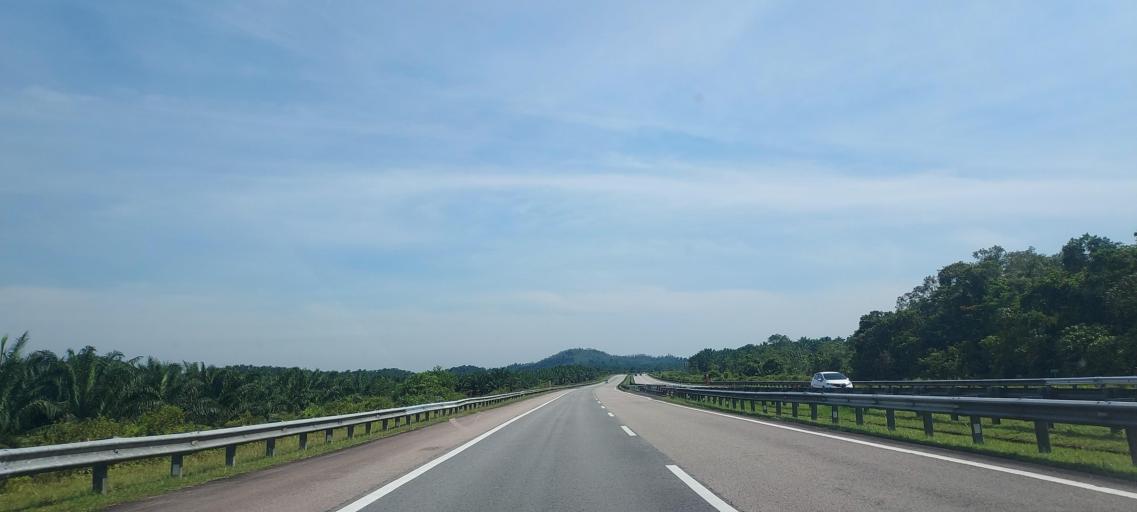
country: MY
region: Terengganu
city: Marang
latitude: 4.9575
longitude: 103.0834
